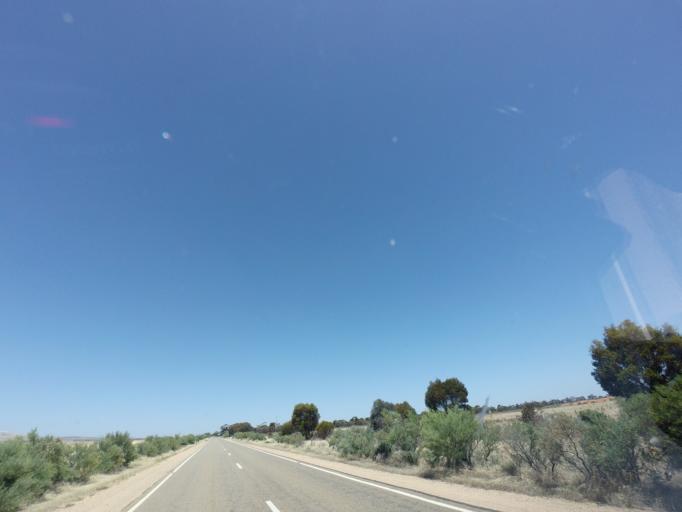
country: AU
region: South Australia
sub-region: Flinders Ranges
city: Quorn
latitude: -32.6854
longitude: 138.3217
